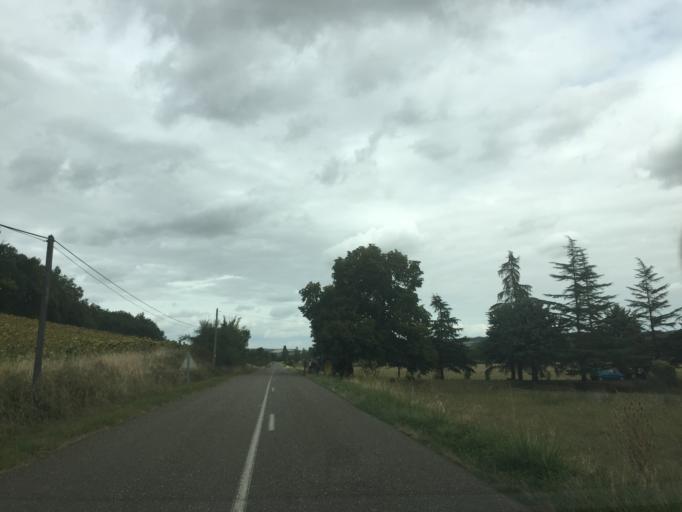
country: FR
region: Midi-Pyrenees
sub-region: Departement du Gers
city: Vic-Fezensac
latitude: 43.7591
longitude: 0.3746
